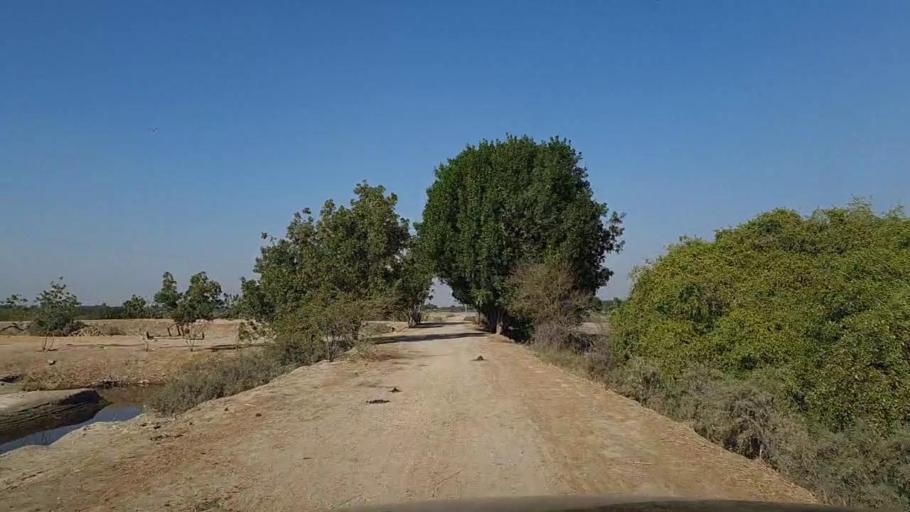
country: PK
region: Sindh
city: Mirpur Batoro
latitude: 24.7458
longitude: 68.3416
